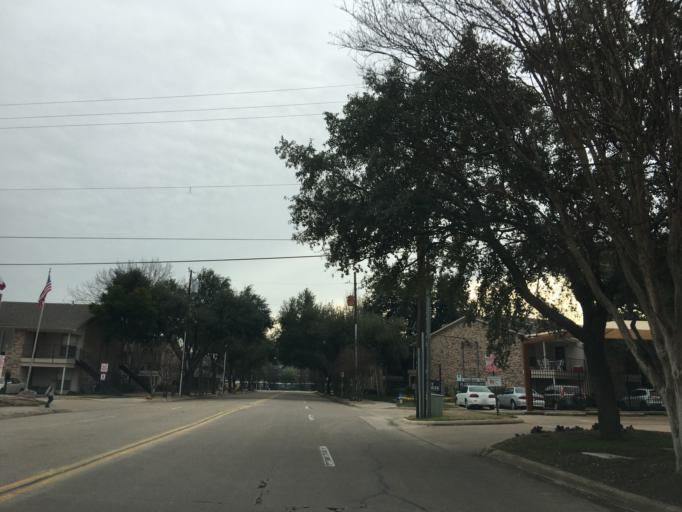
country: US
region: Texas
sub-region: Collin County
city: McKinney
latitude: 33.1980
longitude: -96.6350
